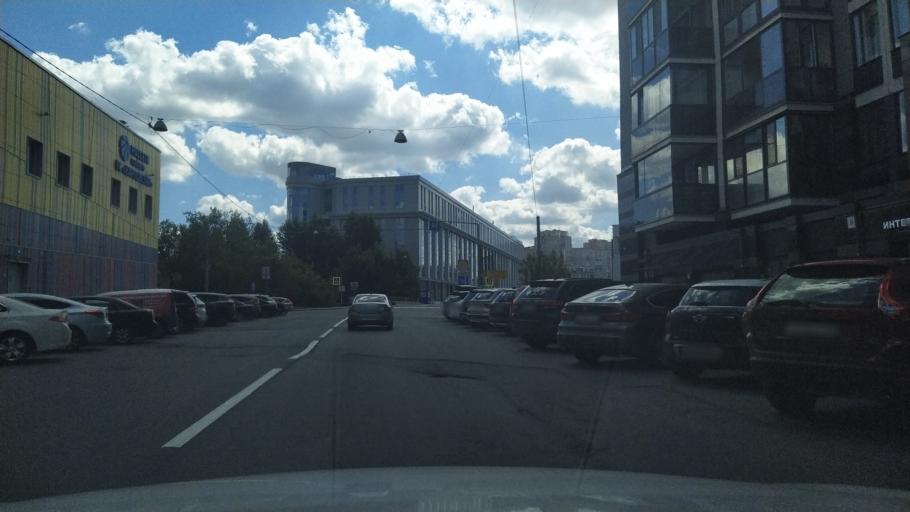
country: RU
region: St.-Petersburg
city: Novaya Derevnya
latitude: 59.9696
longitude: 30.2881
